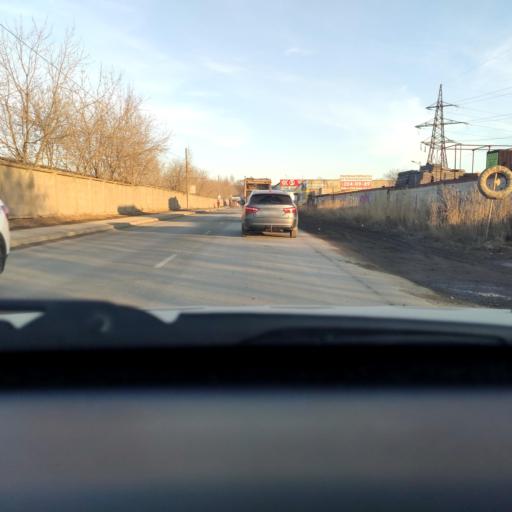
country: RU
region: Perm
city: Froly
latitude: 57.9524
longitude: 56.2602
